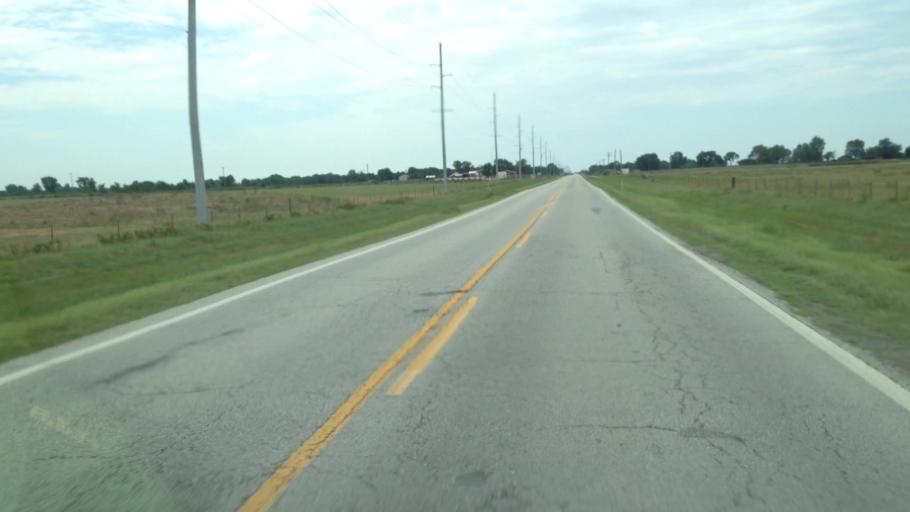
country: US
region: Kansas
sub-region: Labette County
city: Chetopa
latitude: 36.8991
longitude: -95.0895
